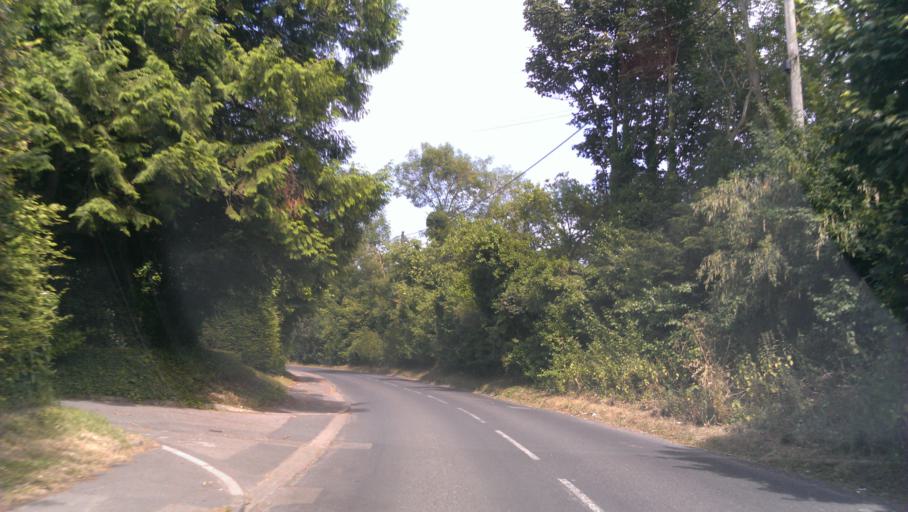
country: GB
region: England
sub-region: Kent
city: Faversham
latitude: 51.3031
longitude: 0.8785
